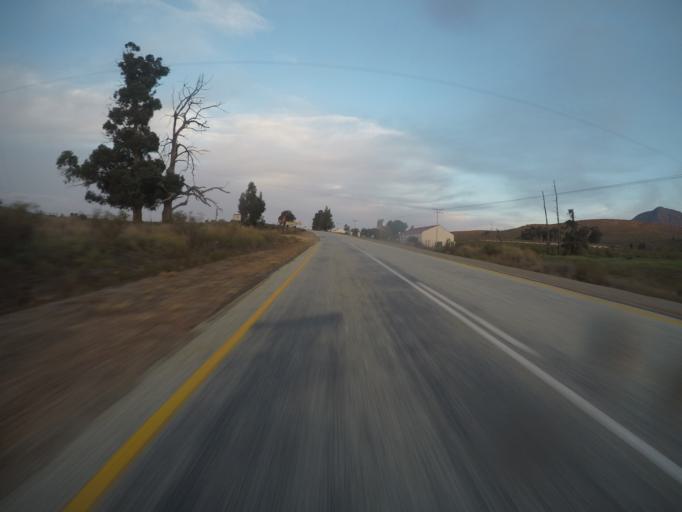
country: ZA
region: Western Cape
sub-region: Eden District Municipality
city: Plettenberg Bay
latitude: -33.7357
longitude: 23.4097
